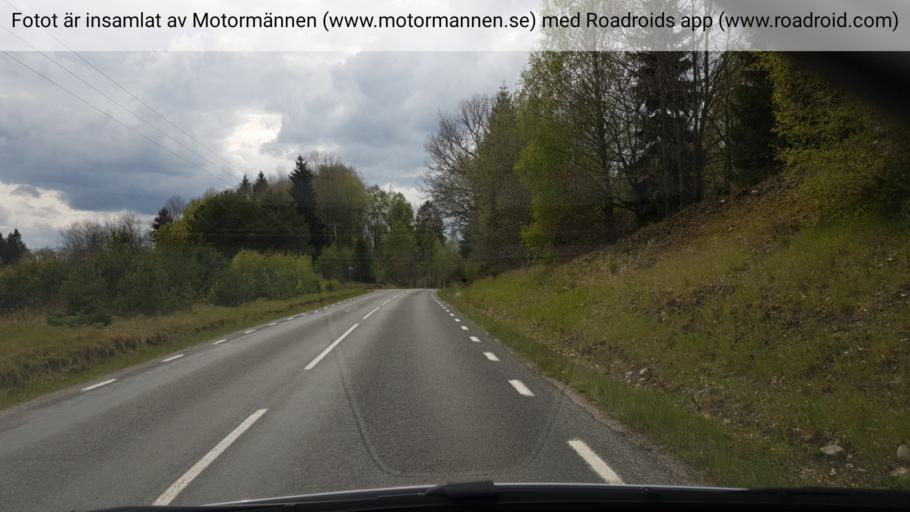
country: SE
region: Vaestra Goetaland
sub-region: Falkopings Kommun
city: Floby
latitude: 58.2356
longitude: 13.4253
